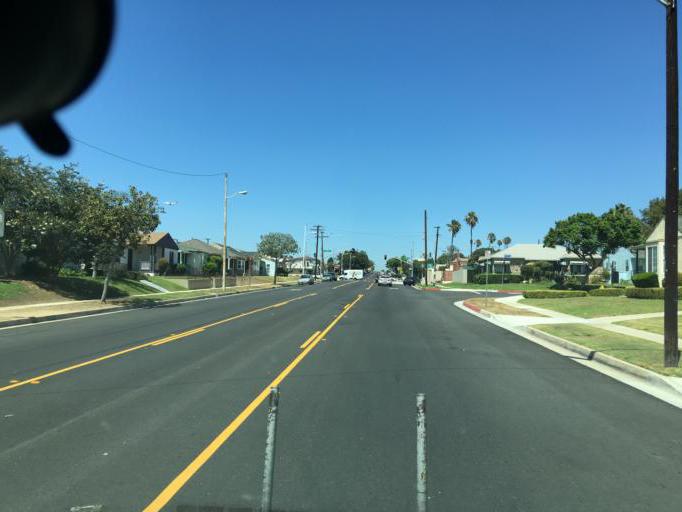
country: US
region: California
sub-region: Los Angeles County
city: Westmont
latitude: 33.9368
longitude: -118.3178
